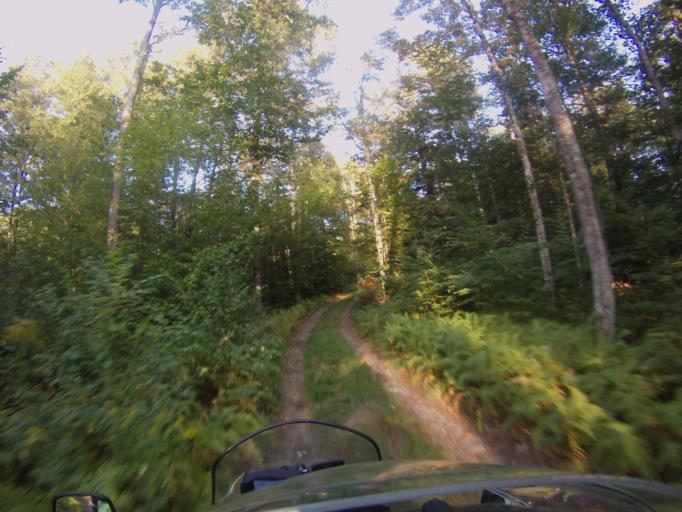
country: US
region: Vermont
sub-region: Addison County
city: Bristol
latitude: 44.0115
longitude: -72.9977
